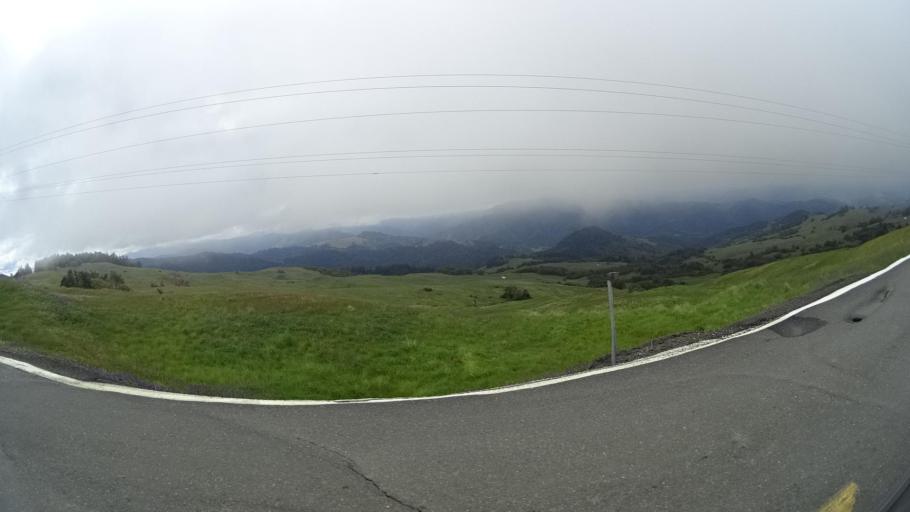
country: US
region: California
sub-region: Humboldt County
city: Redway
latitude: 40.1031
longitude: -123.6912
